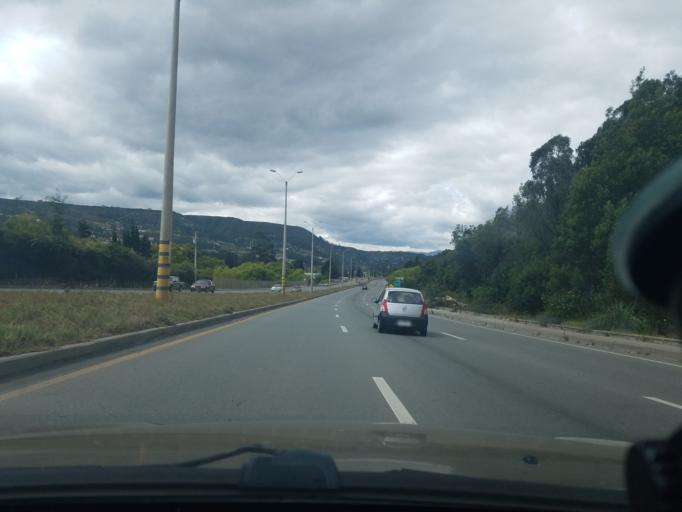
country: EC
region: Azuay
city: Llacao
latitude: -2.8681
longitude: -78.9358
